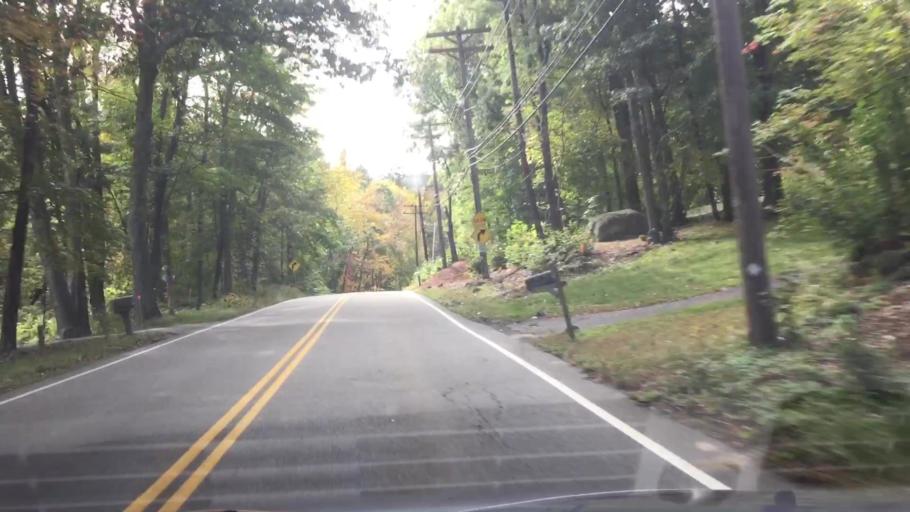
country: US
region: Massachusetts
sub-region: Middlesex County
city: Tewksbury
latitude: 42.6674
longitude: -71.2336
